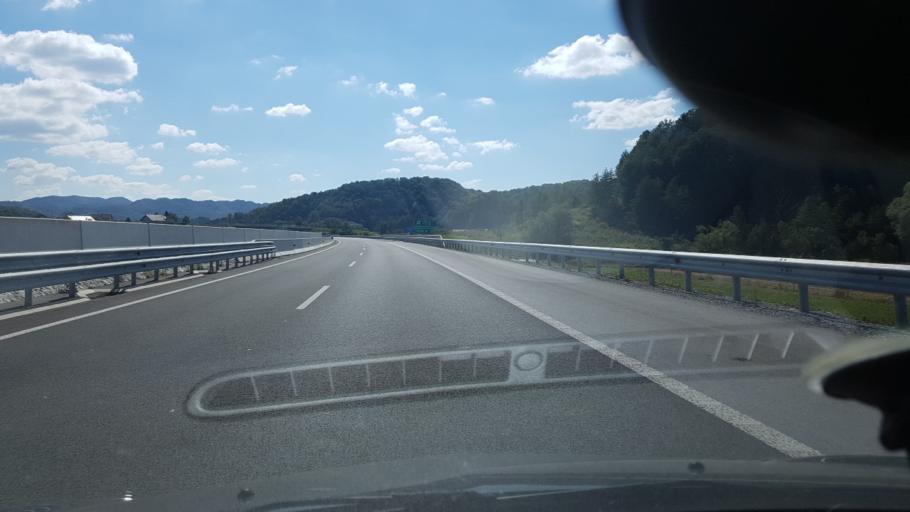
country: SI
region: Podlehnik
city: Podlehnik
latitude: 46.3545
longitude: 15.8681
